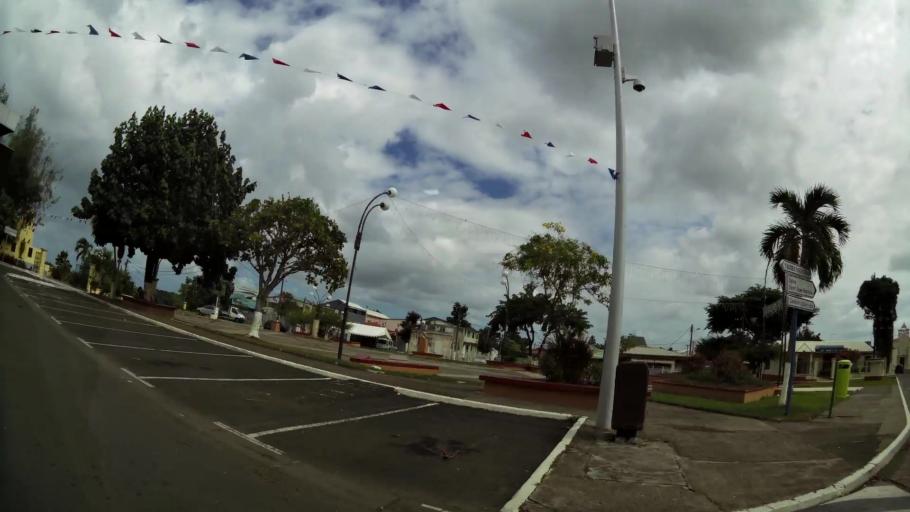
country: GP
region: Guadeloupe
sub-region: Guadeloupe
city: Baie-Mahault
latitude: 16.2683
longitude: -61.5872
